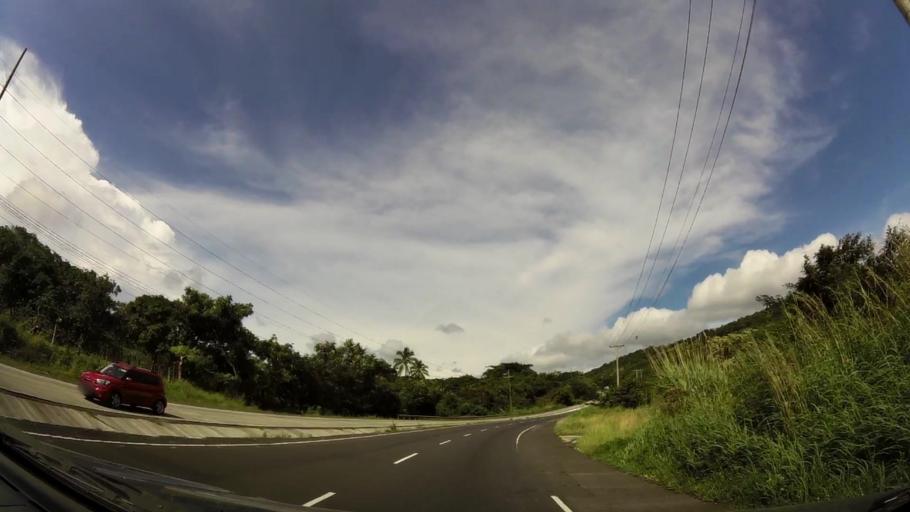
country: PA
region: Panama
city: Bejuco
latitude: 8.6736
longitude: -79.8705
